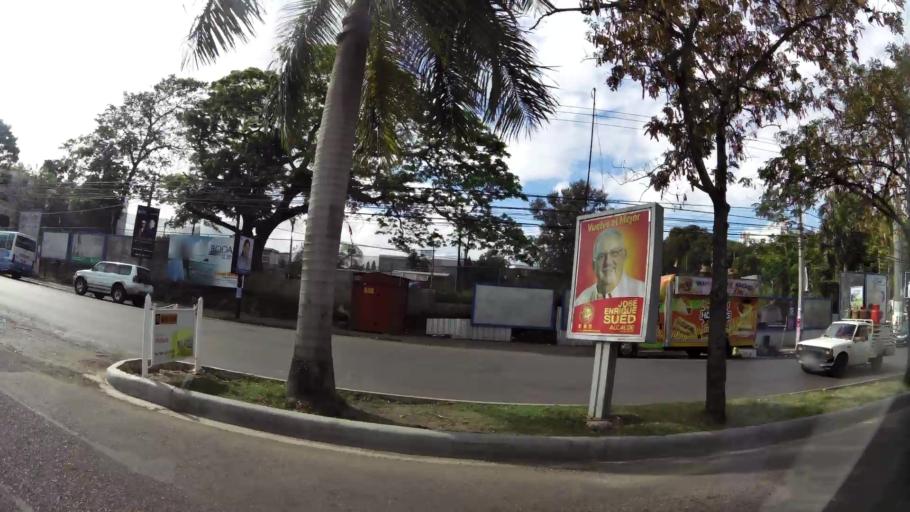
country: DO
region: Santiago
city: Santiago de los Caballeros
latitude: 19.4607
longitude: -70.6841
